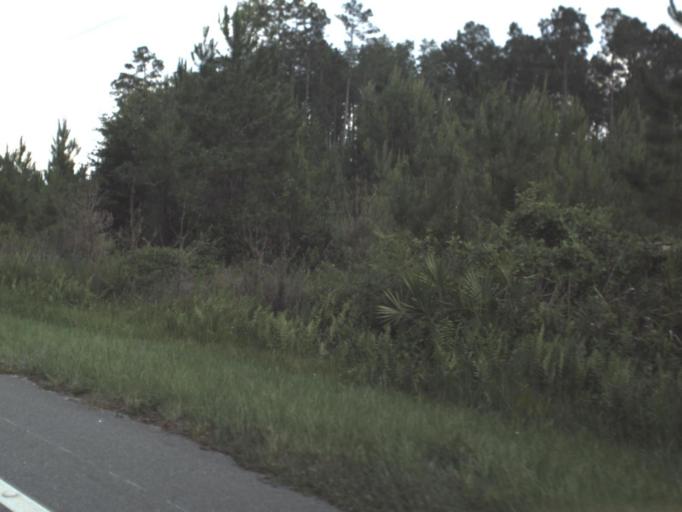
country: US
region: Florida
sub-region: Putnam County
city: Palatka
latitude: 29.6860
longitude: -81.7372
